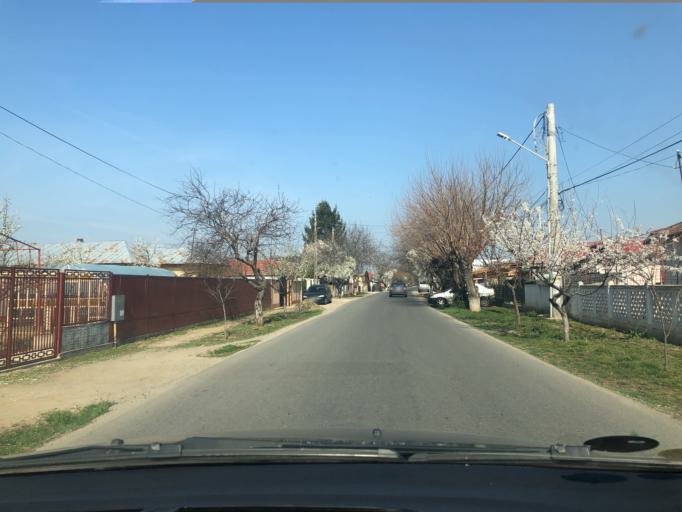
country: RO
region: Ilfov
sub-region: Comuna Clinceni
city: Clinceni
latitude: 44.3737
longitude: 25.9552
